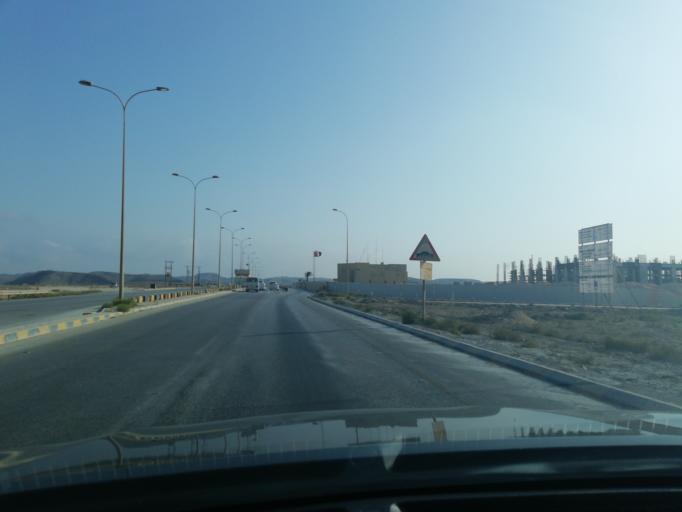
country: OM
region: Zufar
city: Salalah
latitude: 17.2798
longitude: 54.0866
